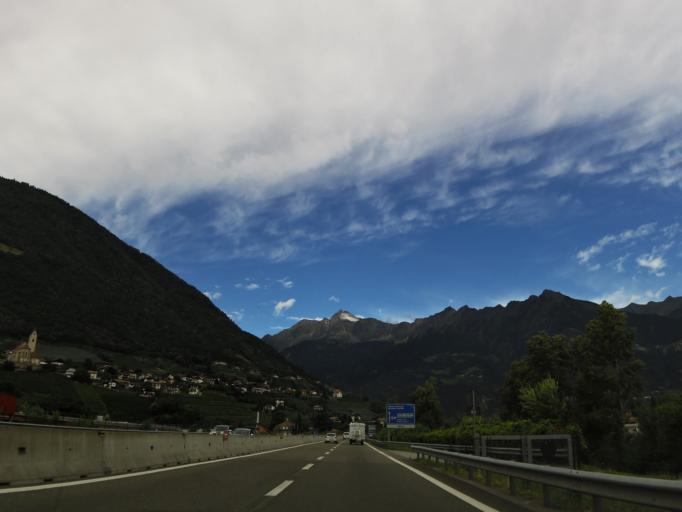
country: IT
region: Trentino-Alto Adige
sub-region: Bolzano
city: Marlengo
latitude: 46.6536
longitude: 11.1499
